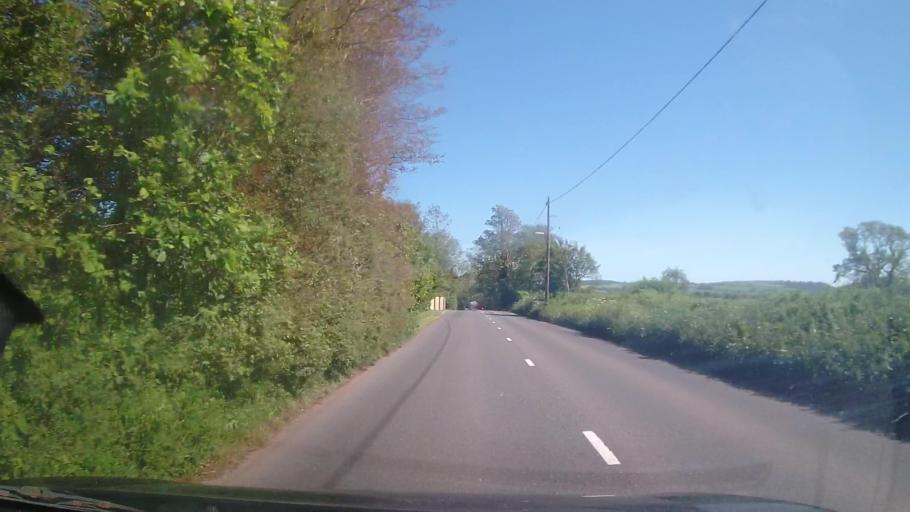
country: GB
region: England
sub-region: Borough of Torbay
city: Paignton
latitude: 50.4091
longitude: -3.5747
